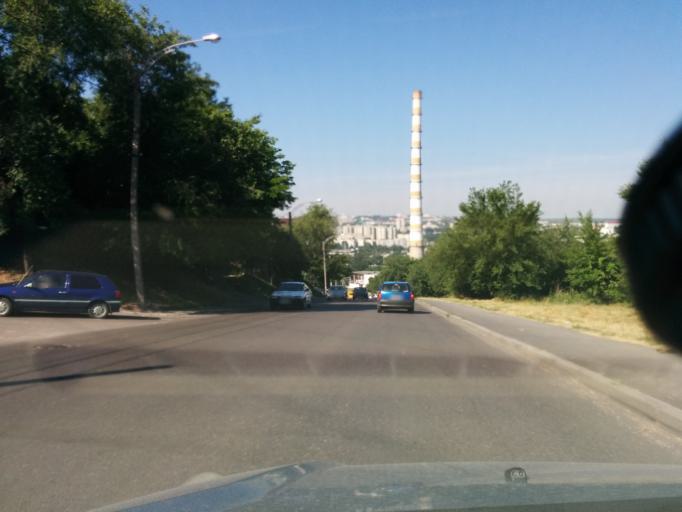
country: MD
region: Chisinau
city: Chisinau
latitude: 47.0278
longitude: 28.8736
